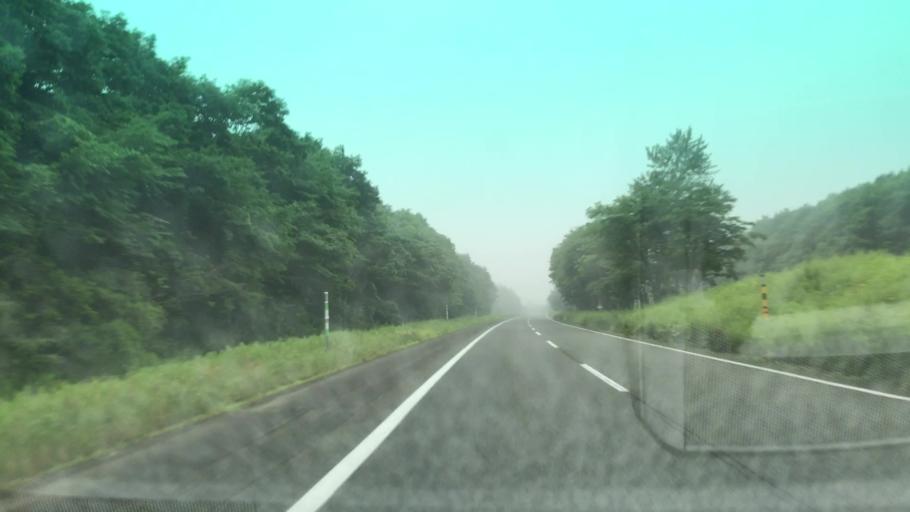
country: JP
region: Hokkaido
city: Chitose
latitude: 42.7927
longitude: 141.6270
